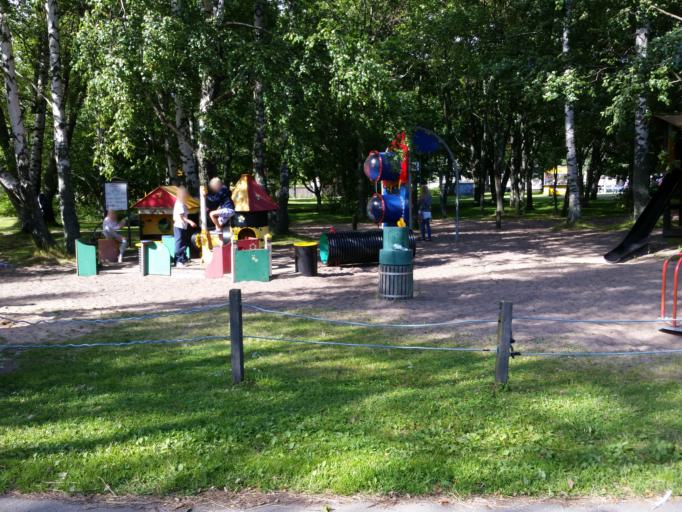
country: FI
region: Uusimaa
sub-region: Raaseporin
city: Hanko
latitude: 59.8207
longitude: 22.9675
